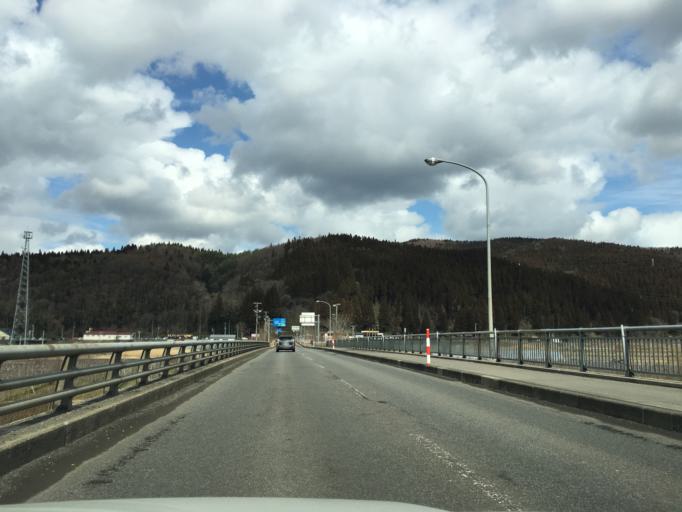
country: JP
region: Akita
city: Odate
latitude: 40.2271
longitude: 140.5906
